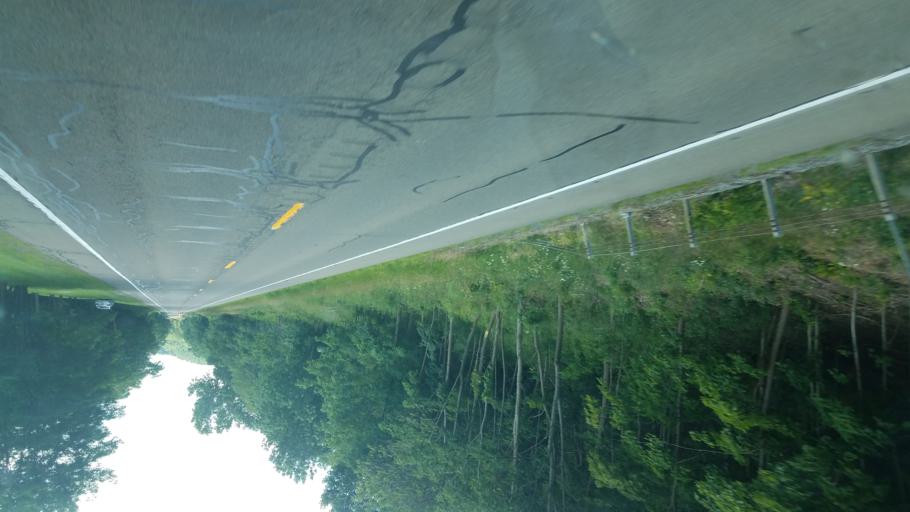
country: US
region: New York
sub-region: Steuben County
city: Sylvan Beach
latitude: 42.5284
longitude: -77.1002
